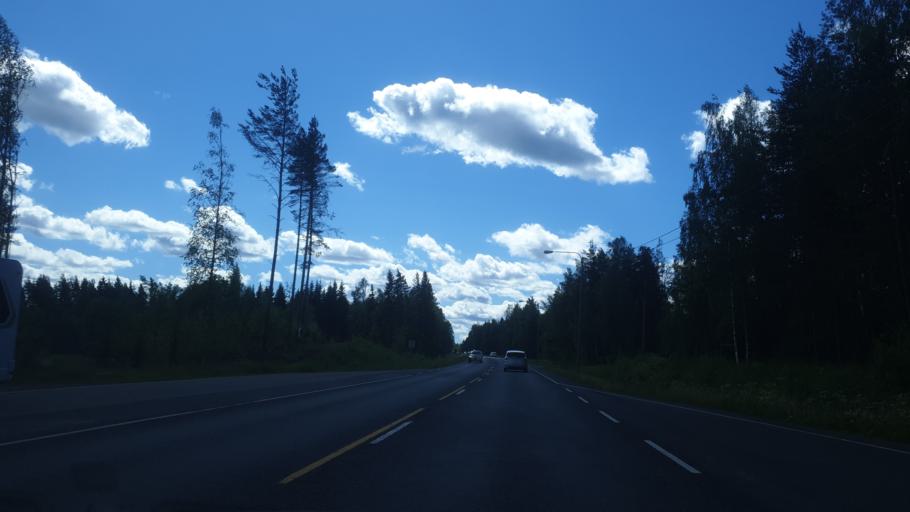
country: FI
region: Northern Savo
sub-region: Varkaus
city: Leppaevirta
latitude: 62.5929
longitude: 27.6054
